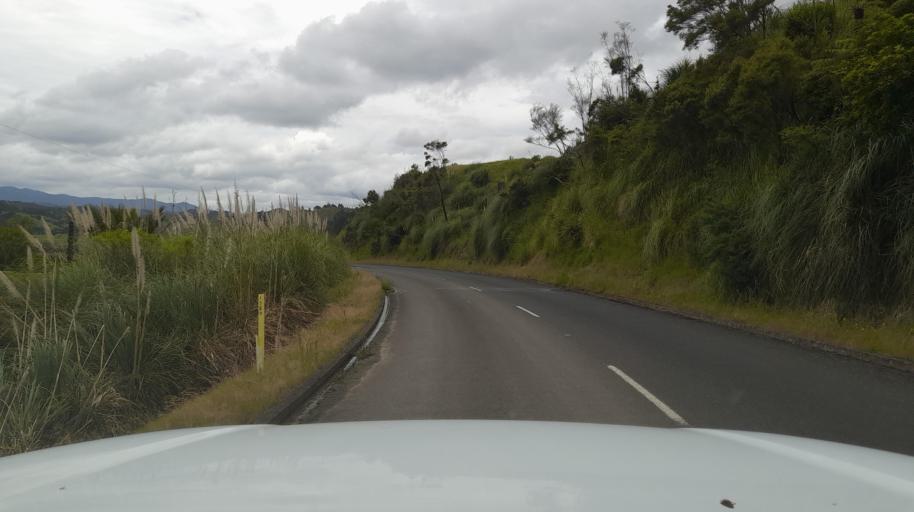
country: NZ
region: Northland
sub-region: Far North District
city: Kaitaia
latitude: -35.3680
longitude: 173.4322
